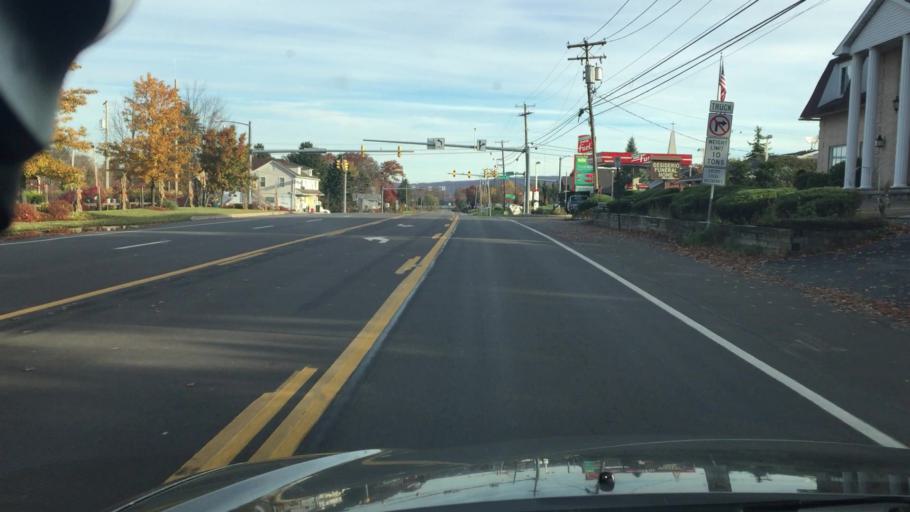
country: US
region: Pennsylvania
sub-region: Luzerne County
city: Mountain Top
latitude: 41.1192
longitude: -75.9103
